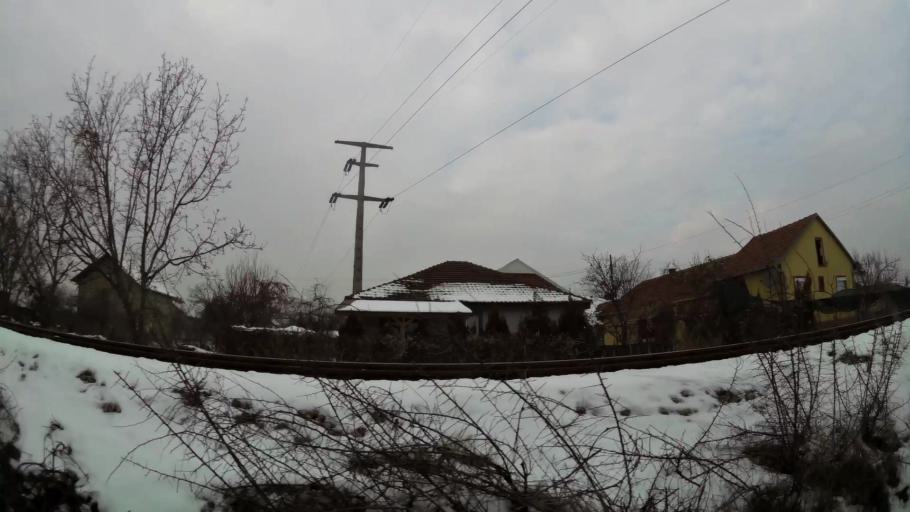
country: MK
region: Saraj
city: Saraj
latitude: 42.0409
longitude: 21.3525
